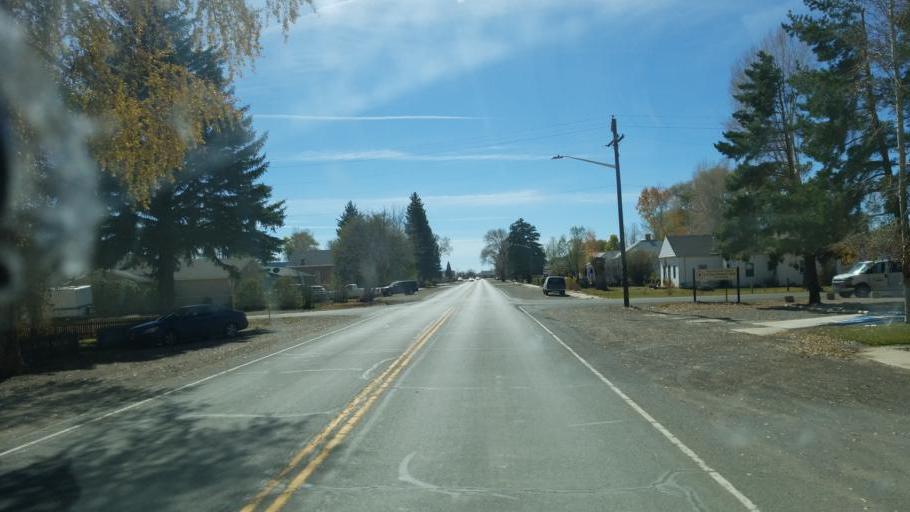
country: US
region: Colorado
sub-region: Conejos County
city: Conejos
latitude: 37.2731
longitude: -105.9597
